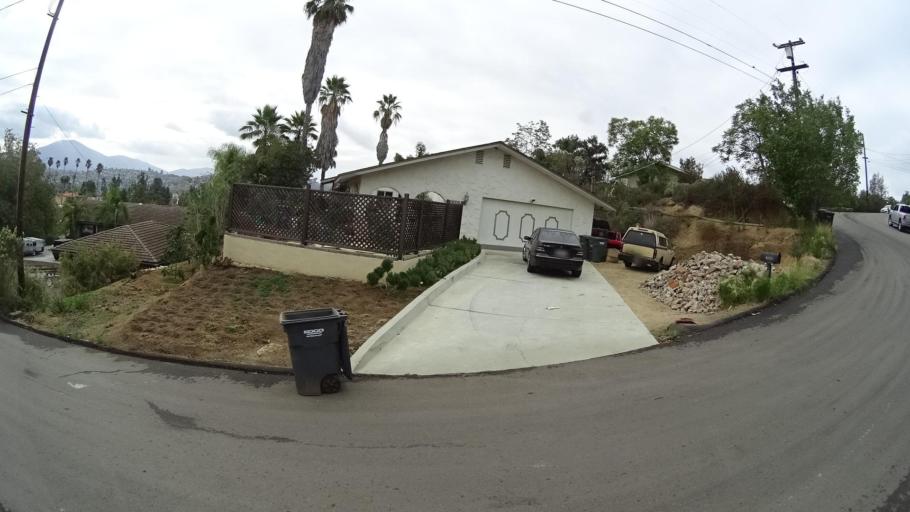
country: US
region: California
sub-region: San Diego County
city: Spring Valley
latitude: 32.7574
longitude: -116.9889
